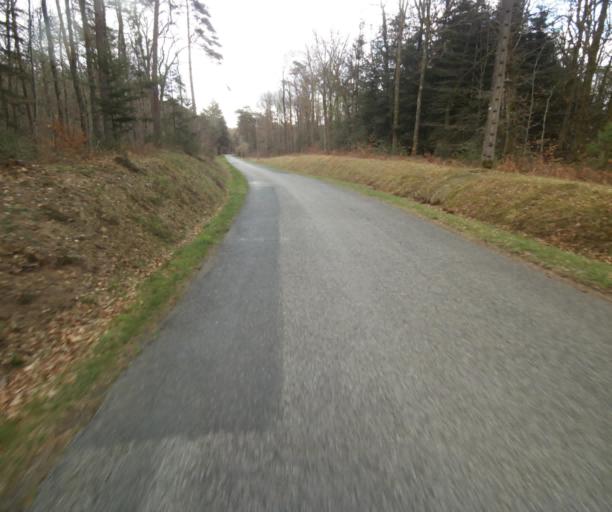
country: FR
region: Limousin
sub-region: Departement de la Correze
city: Correze
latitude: 45.2489
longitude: 1.9319
